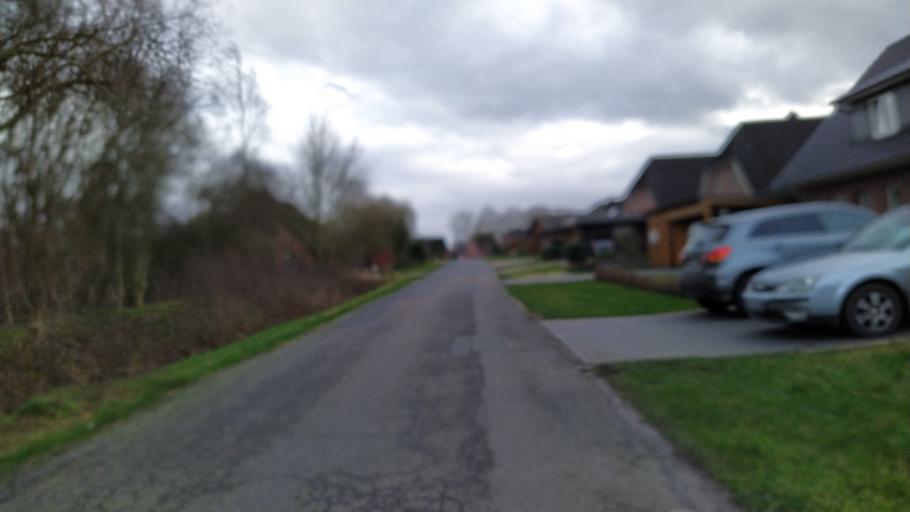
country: DE
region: Lower Saxony
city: Bargstedt
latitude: 53.4396
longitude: 9.4677
